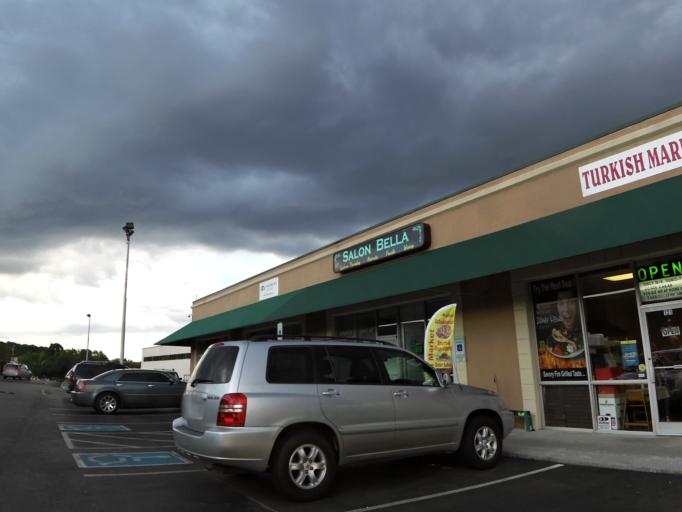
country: US
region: Tennessee
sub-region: Blount County
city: Louisville
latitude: 35.9238
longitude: -84.0501
